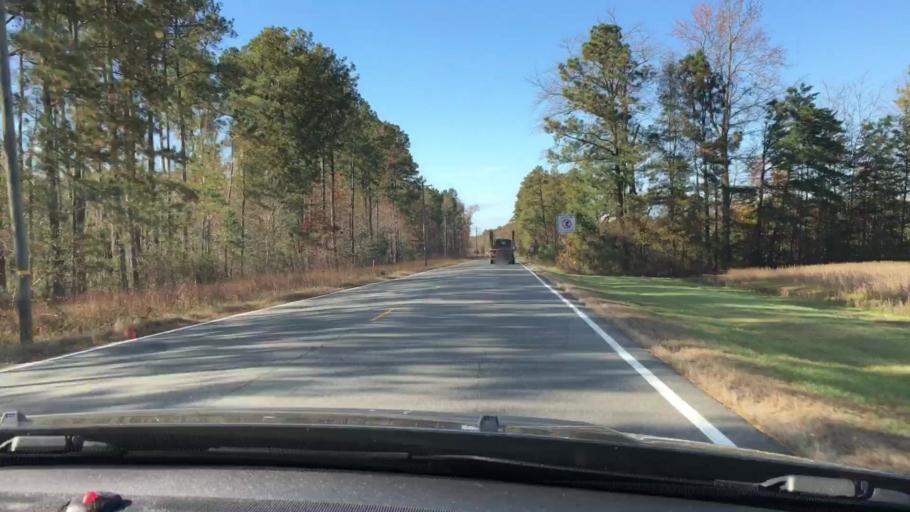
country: US
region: Virginia
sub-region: Hanover County
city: Hanover
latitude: 37.8191
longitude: -77.3197
